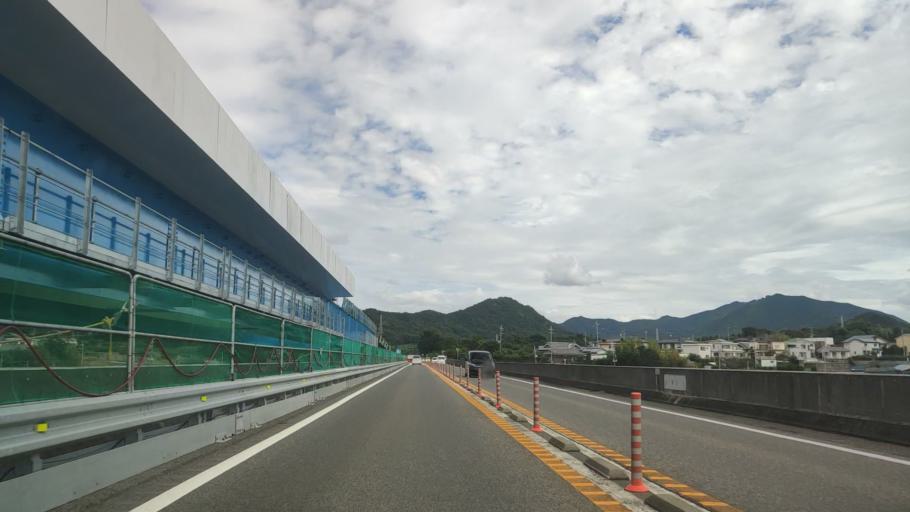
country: JP
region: Wakayama
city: Gobo
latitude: 33.9036
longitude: 135.1896
